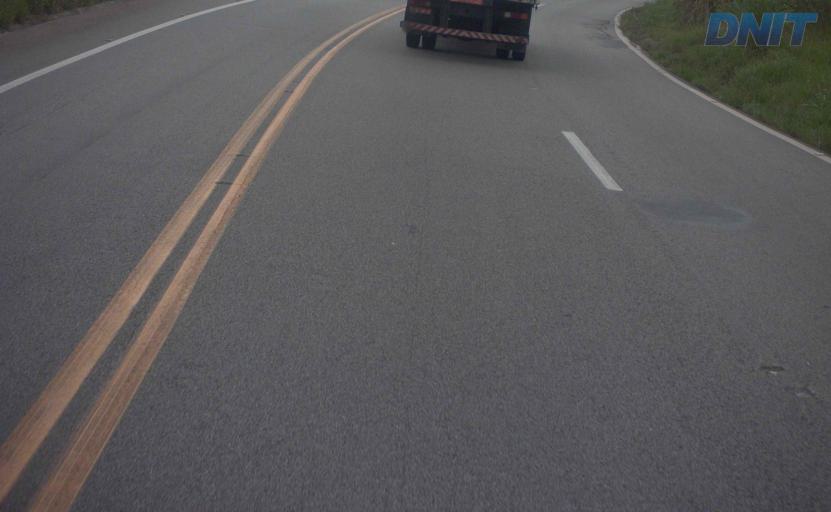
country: BR
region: Minas Gerais
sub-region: Nova Era
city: Nova Era
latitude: -19.6649
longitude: -42.9648
